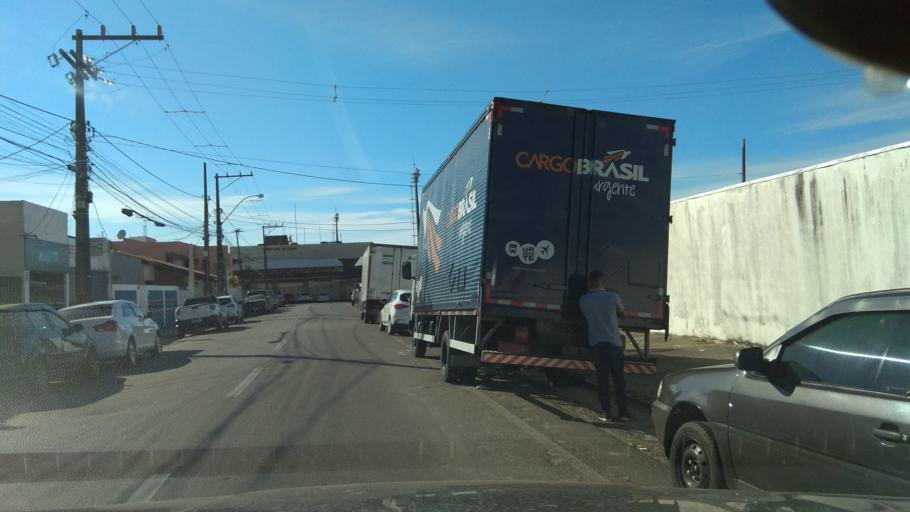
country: BR
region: Bahia
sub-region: Ilheus
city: Ilheus
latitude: -14.8140
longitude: -39.0331
